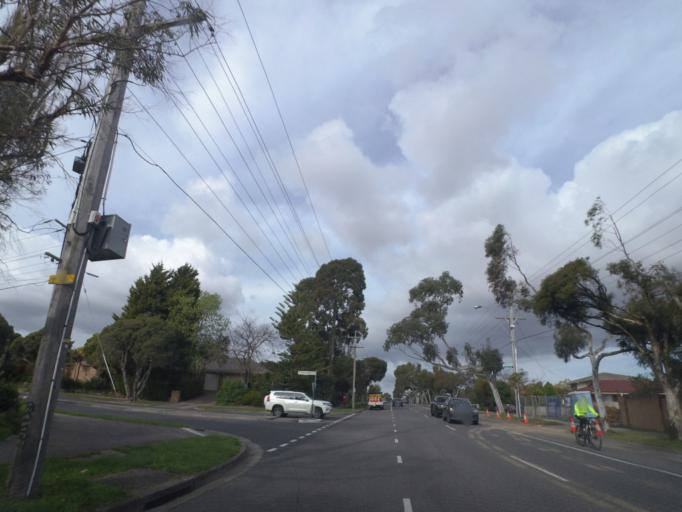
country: AU
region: Victoria
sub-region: Whitehorse
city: Vermont South
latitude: -37.8635
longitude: 145.1820
